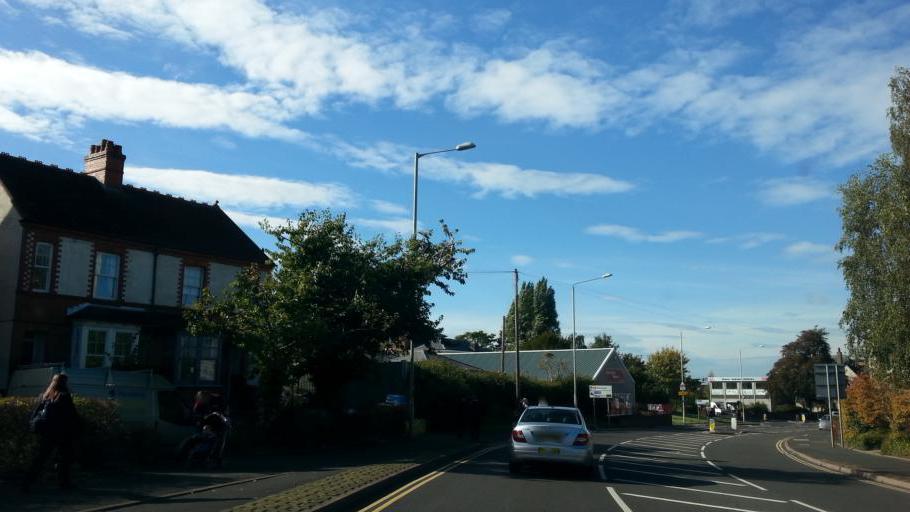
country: GB
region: England
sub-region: Telford and Wrekin
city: Wellington
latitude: 52.6985
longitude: -2.5200
